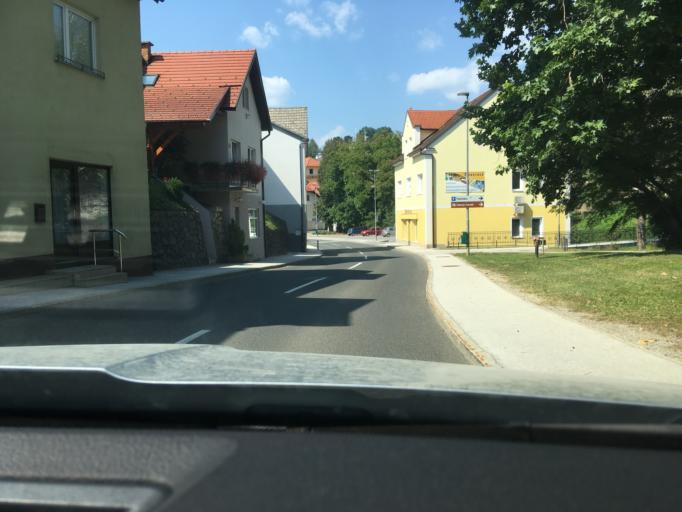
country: SI
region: Metlika
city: Metlika
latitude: 45.6497
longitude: 15.3165
